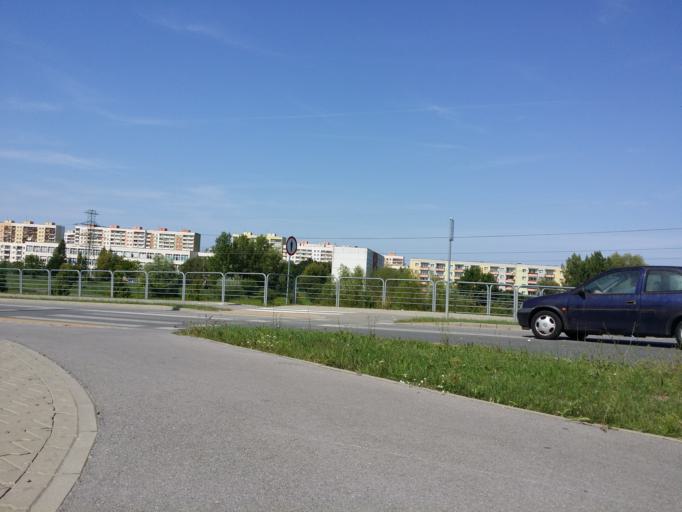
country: PL
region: Masovian Voivodeship
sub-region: Radom
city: Radom
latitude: 51.3761
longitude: 21.1658
